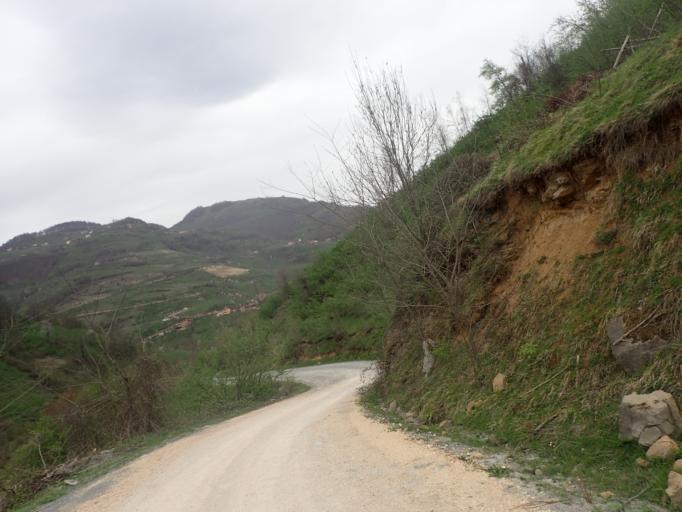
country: TR
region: Ordu
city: Korgan
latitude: 40.7676
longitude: 37.3320
